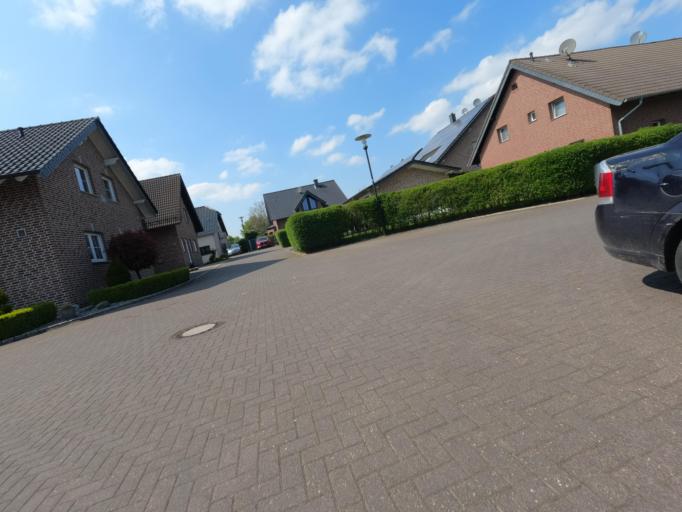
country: DE
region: North Rhine-Westphalia
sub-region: Regierungsbezirk Koln
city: Heinsberg
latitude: 51.0507
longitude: 6.0714
